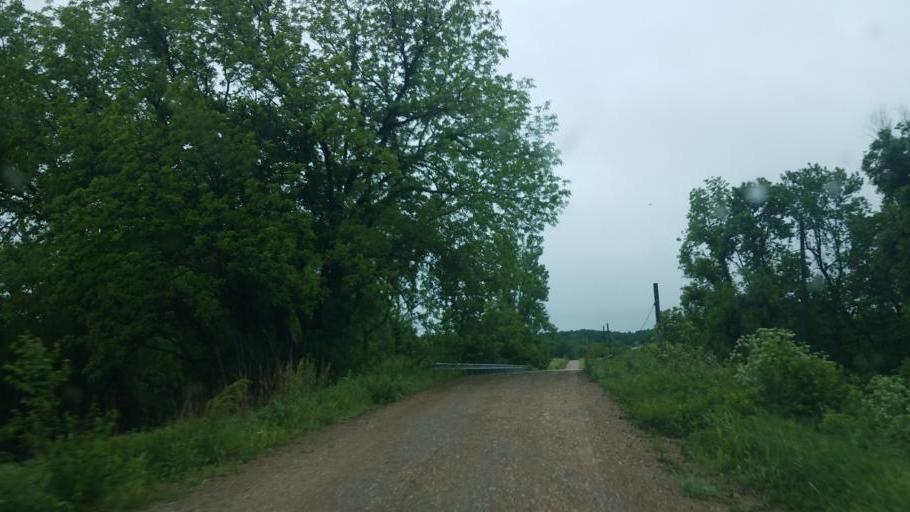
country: US
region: Missouri
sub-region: Moniteau County
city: California
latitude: 38.7318
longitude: -92.6095
